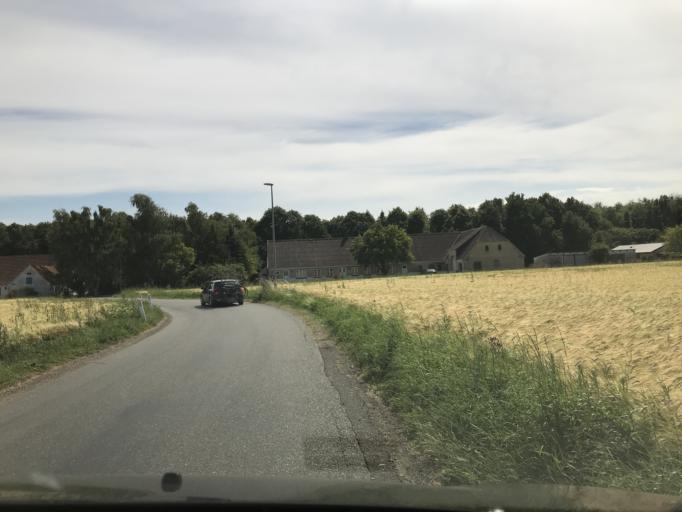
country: DK
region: South Denmark
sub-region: AEro Kommune
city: Marstal
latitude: 54.8486
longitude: 10.5110
